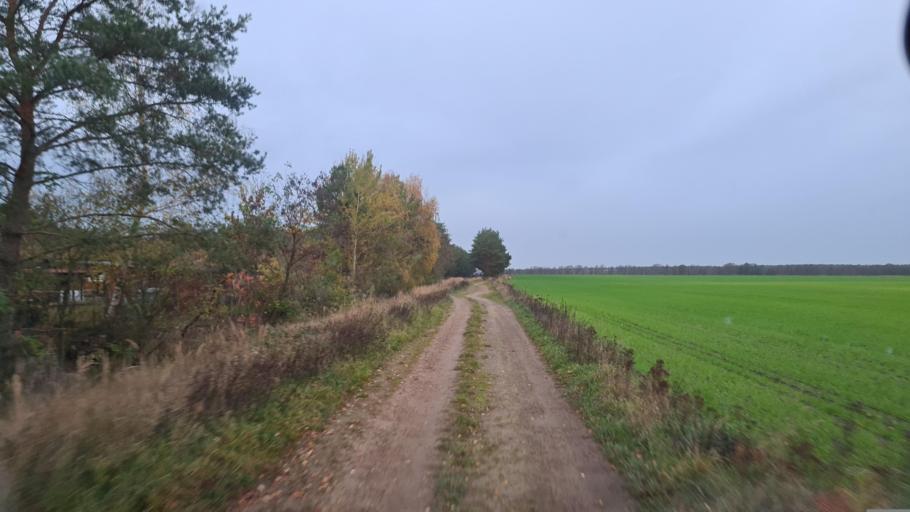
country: DE
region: Saxony-Anhalt
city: Holzdorf
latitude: 51.7873
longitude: 13.1557
